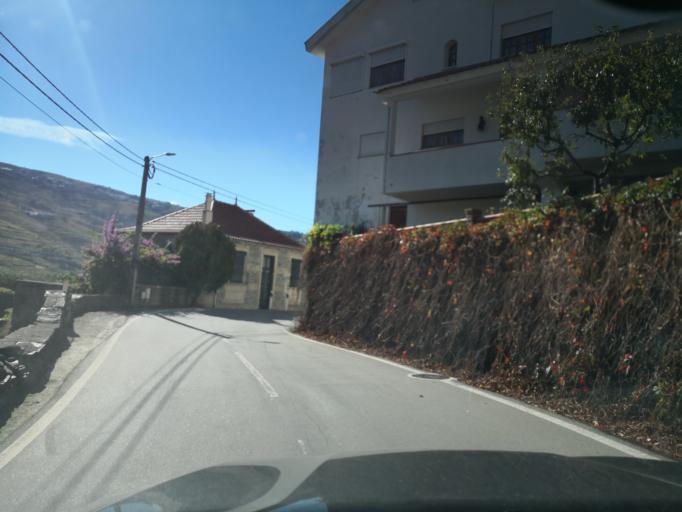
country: PT
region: Viseu
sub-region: Tabuaco
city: Tabuaco
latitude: 41.1704
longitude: -7.5380
